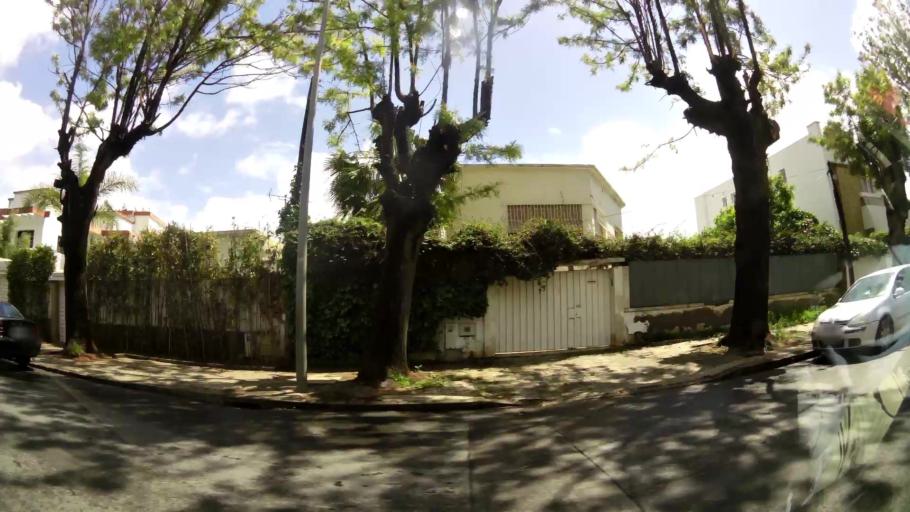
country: MA
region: Grand Casablanca
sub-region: Casablanca
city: Casablanca
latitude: 33.5690
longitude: -7.6407
